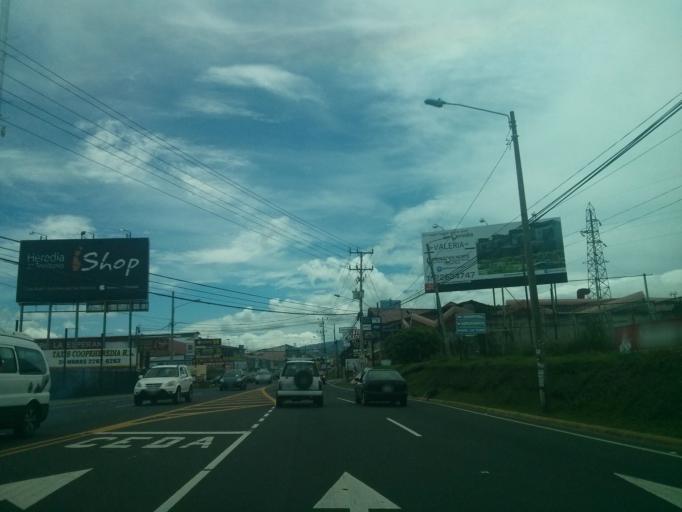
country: CR
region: Heredia
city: Heredia
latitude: 9.9884
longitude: -84.1108
